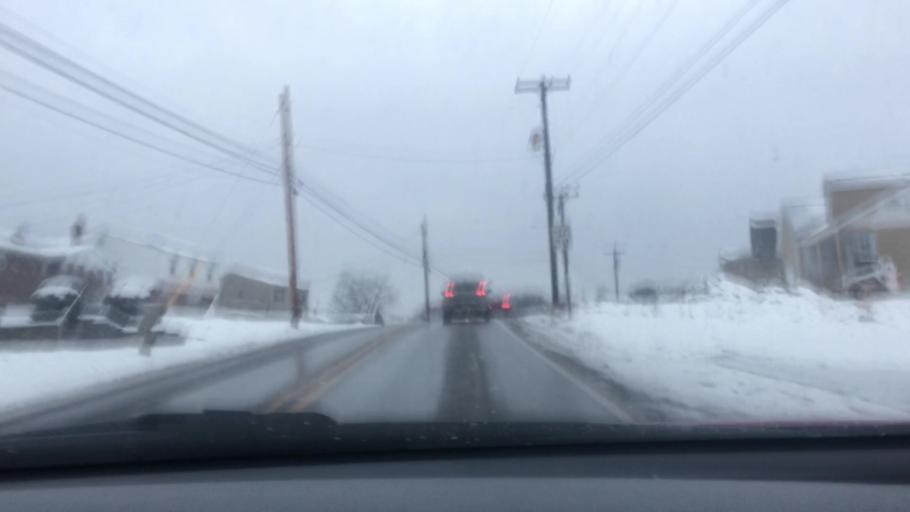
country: US
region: Pennsylvania
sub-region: Allegheny County
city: Bethel Park
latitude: 40.3397
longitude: -80.0207
